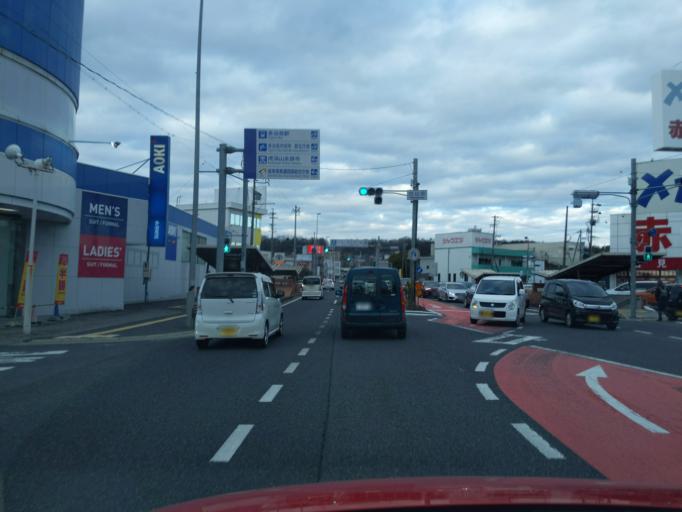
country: JP
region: Gifu
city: Tajimi
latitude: 35.3411
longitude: 137.1189
